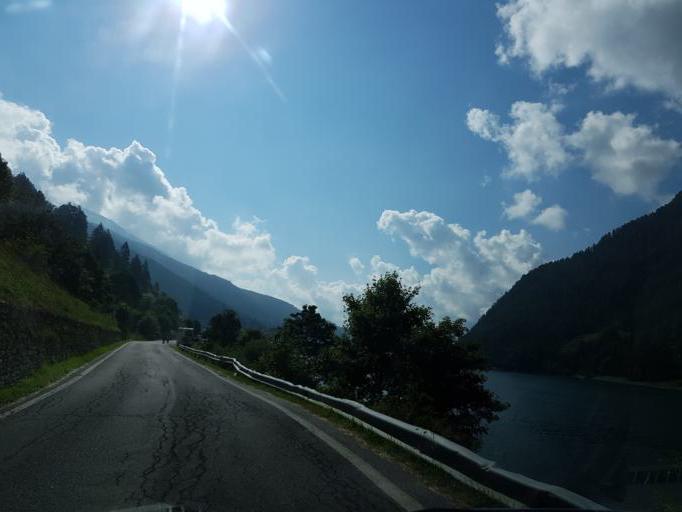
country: IT
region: Piedmont
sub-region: Provincia di Cuneo
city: Pontechianale
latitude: 44.6180
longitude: 7.0387
